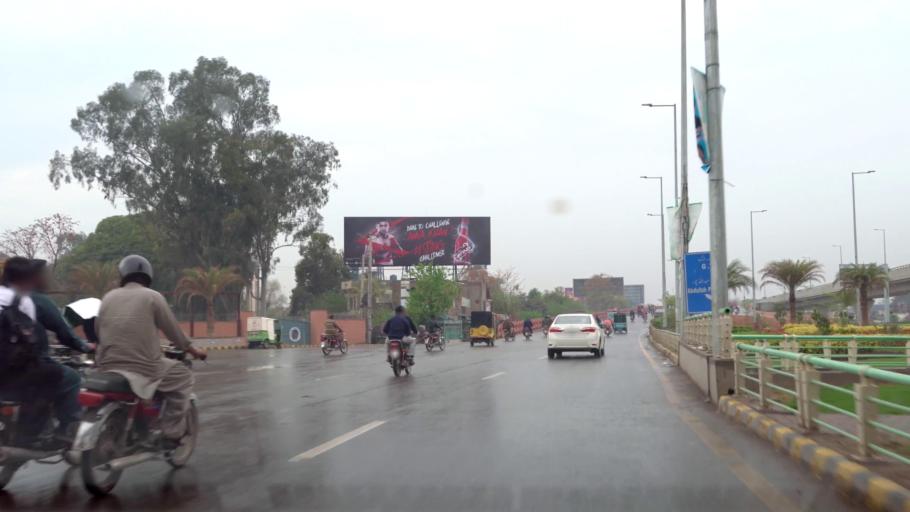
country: PK
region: Punjab
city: Faisalabad
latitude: 31.4089
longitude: 73.0958
